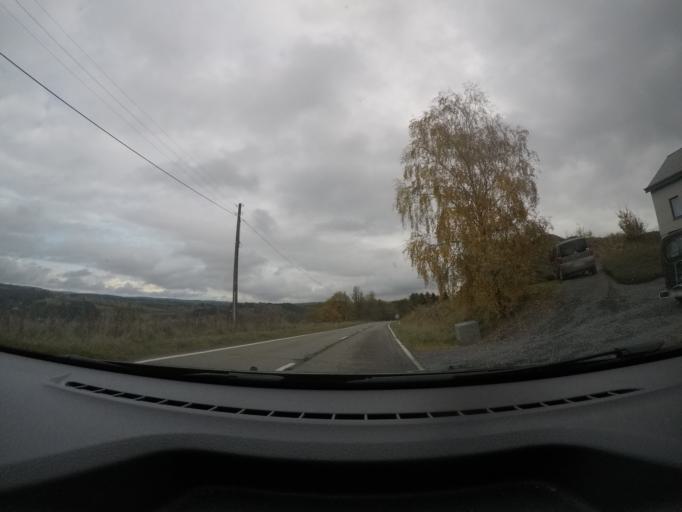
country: BE
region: Wallonia
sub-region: Province du Luxembourg
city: Houffalize
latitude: 50.1481
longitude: 5.7141
